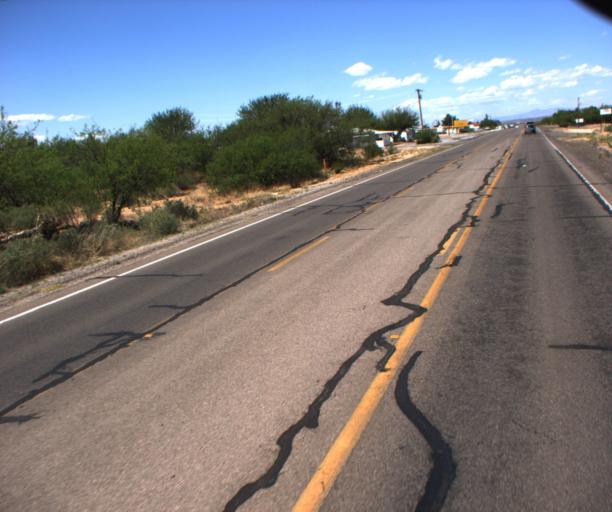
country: US
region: Arizona
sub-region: Cochise County
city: Benson
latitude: 31.9448
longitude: -110.2859
